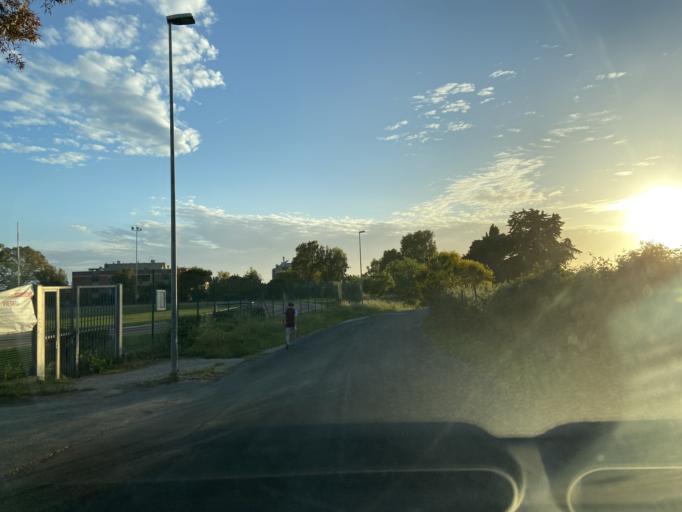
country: IT
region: Latium
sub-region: Citta metropolitana di Roma Capitale
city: Civitavecchia
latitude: 42.0773
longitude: 11.8181
